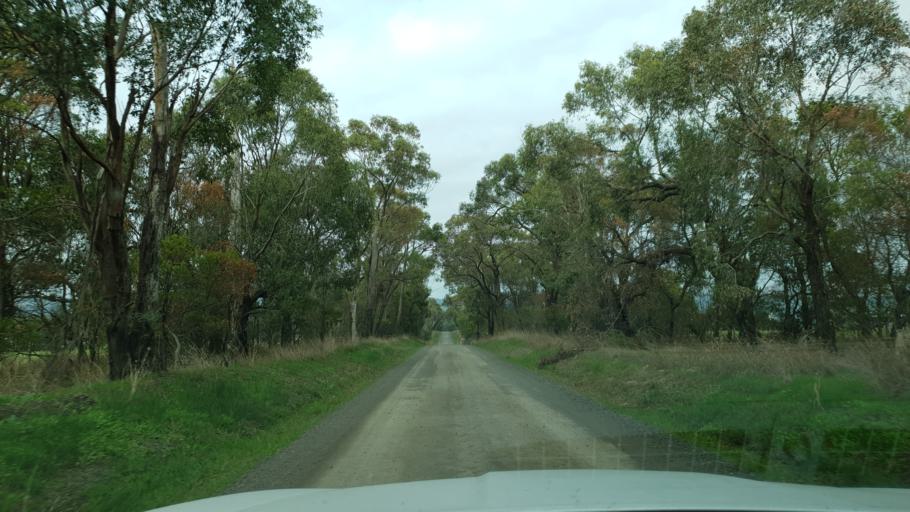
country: AU
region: Victoria
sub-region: Latrobe
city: Moe
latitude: -38.1702
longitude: 146.1312
